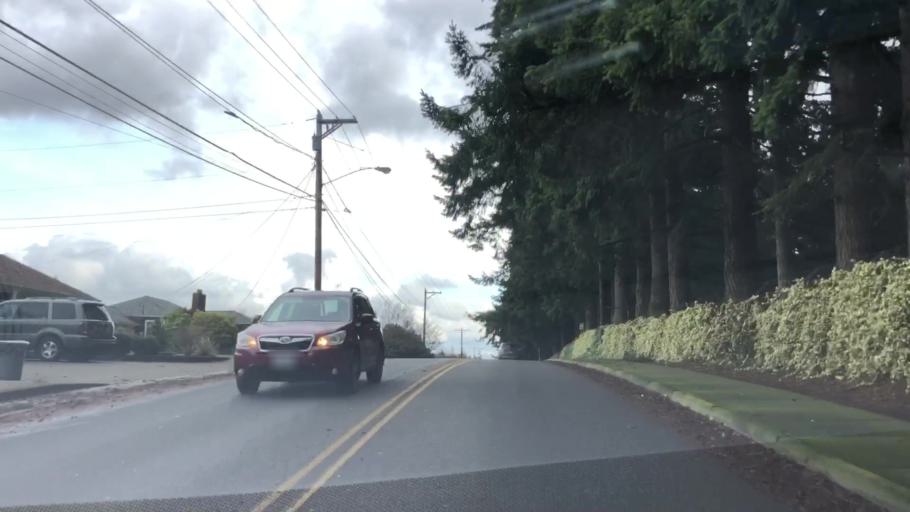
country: US
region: Washington
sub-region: Snohomish County
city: Everett
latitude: 47.9494
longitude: -122.2110
